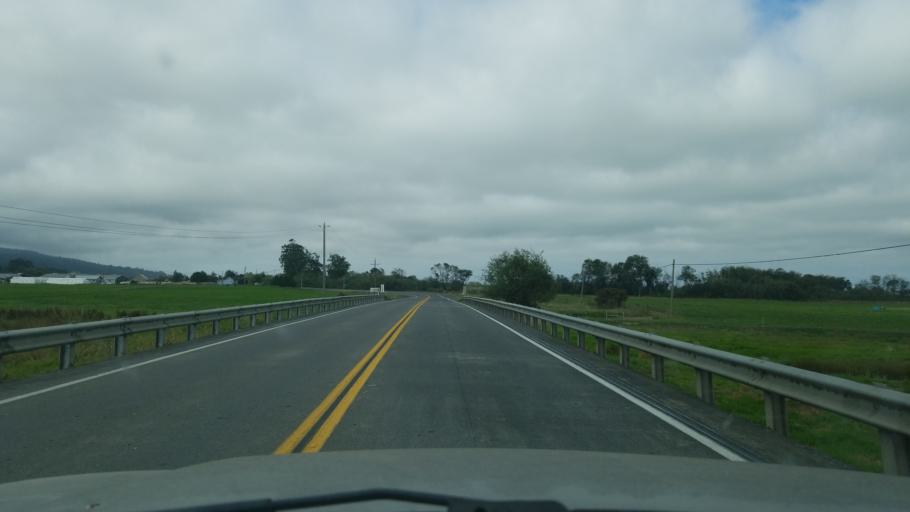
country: US
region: California
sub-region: Humboldt County
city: Ferndale
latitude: 40.5955
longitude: -124.2409
